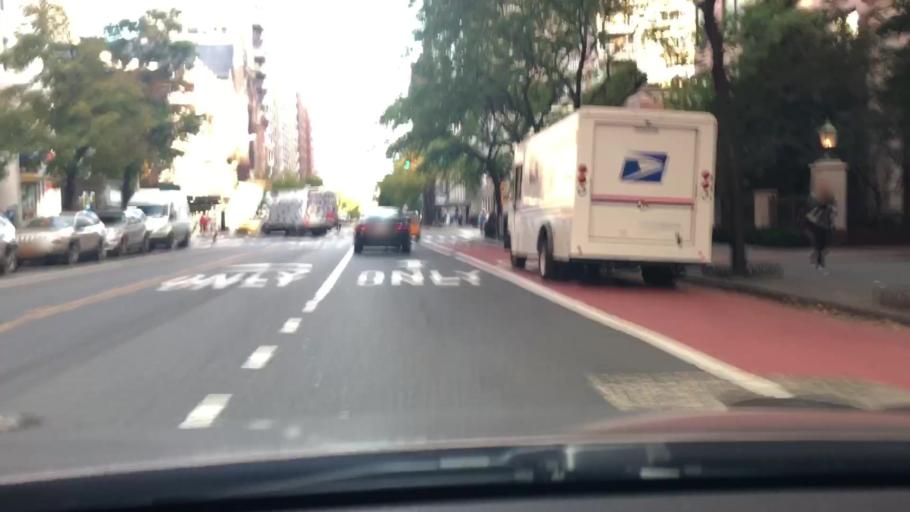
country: US
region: New York
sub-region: New York County
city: Manhattan
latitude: 40.7726
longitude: -73.9534
